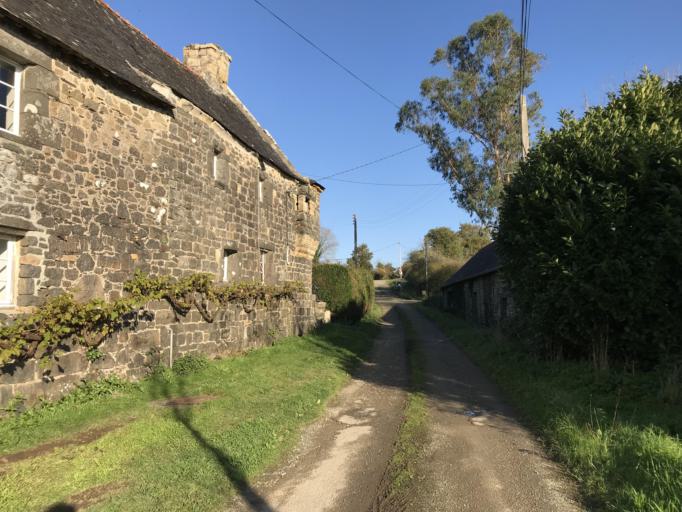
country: FR
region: Brittany
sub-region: Departement du Finistere
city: Hopital-Camfrout
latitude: 48.3146
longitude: -4.2296
